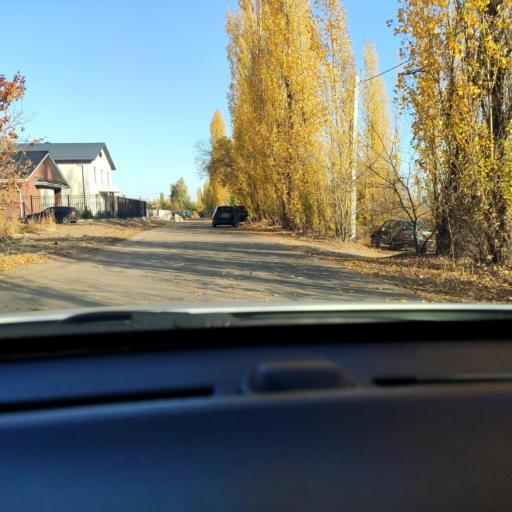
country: RU
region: Voronezj
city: Voronezh
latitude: 51.7059
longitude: 39.2386
